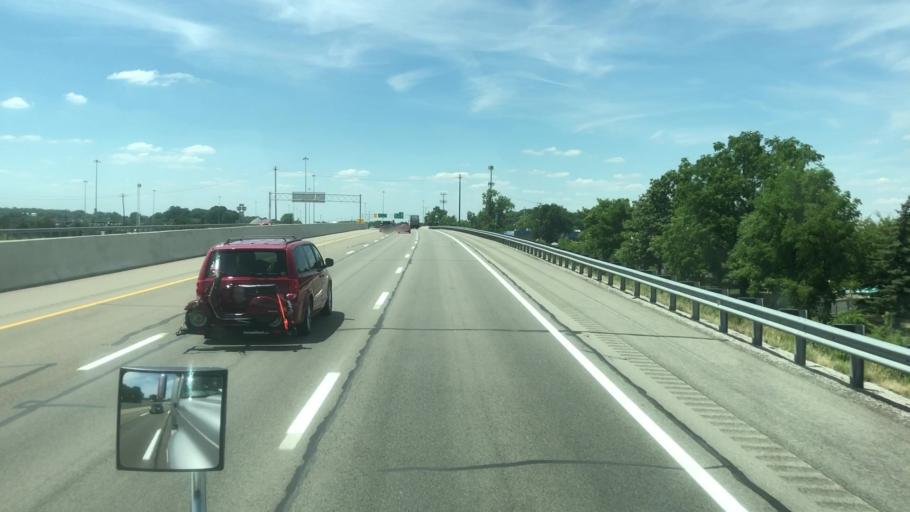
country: US
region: Ohio
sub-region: Lucas County
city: Maumee
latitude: 41.5917
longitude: -83.6609
